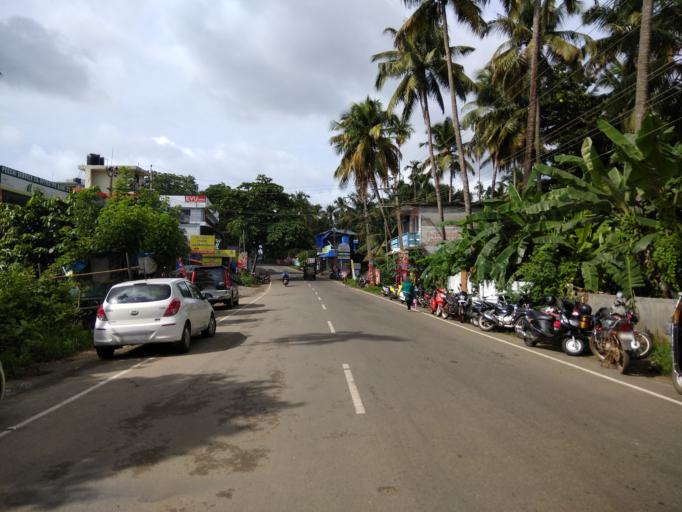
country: IN
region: Kerala
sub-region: Thrissur District
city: Trichur
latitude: 10.5557
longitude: 76.3236
